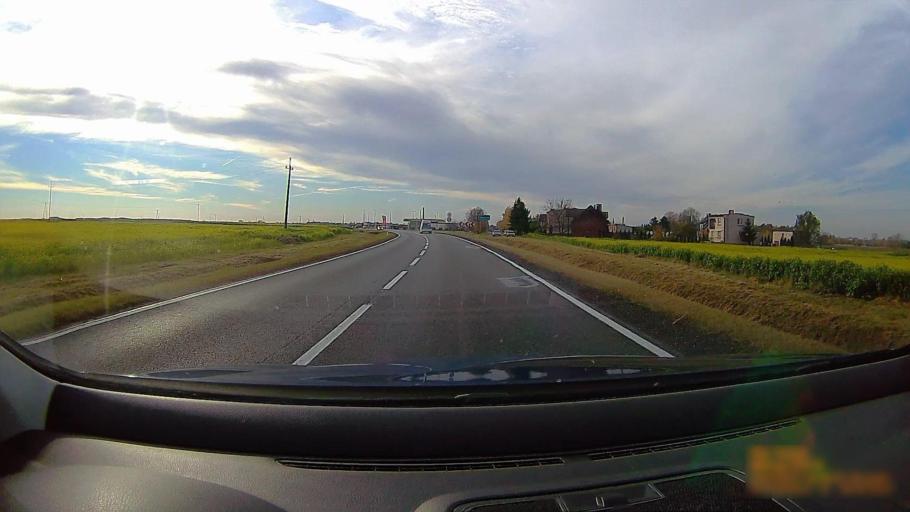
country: PL
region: Greater Poland Voivodeship
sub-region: Powiat kaliski
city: Stawiszyn
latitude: 51.9291
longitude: 18.1202
